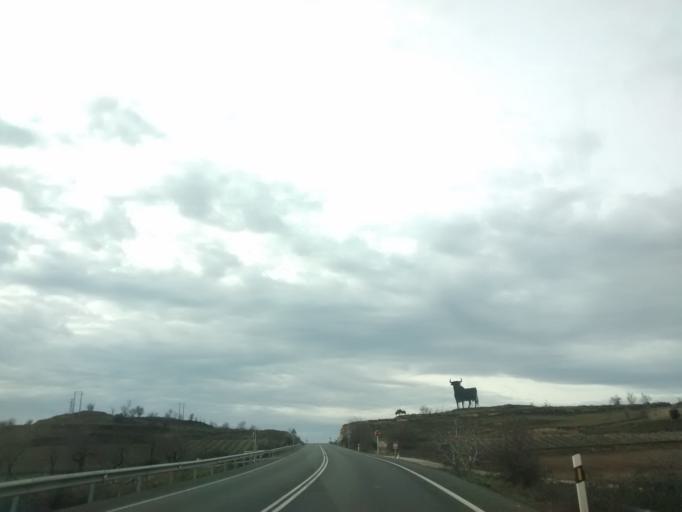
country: ES
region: La Rioja
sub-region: Provincia de La Rioja
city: San Asensio
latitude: 42.5105
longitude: -2.7195
